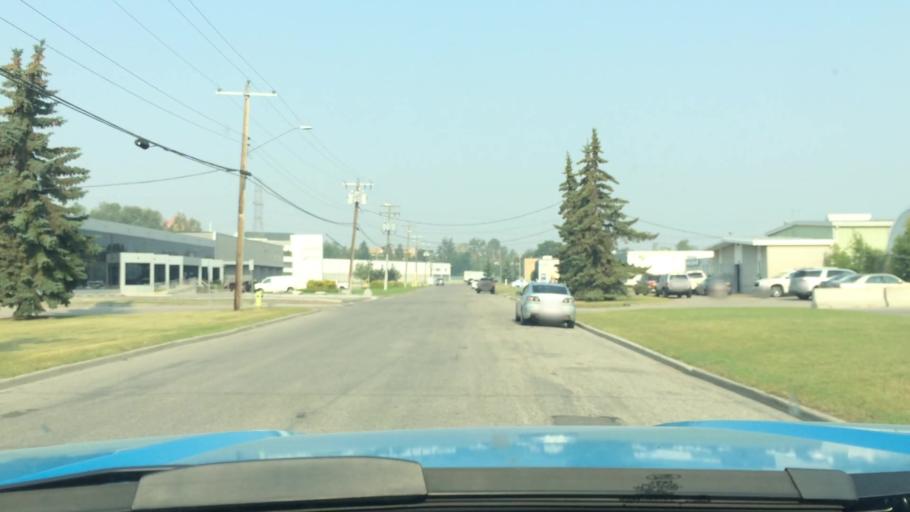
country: CA
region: Alberta
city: Calgary
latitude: 51.0107
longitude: -114.0536
